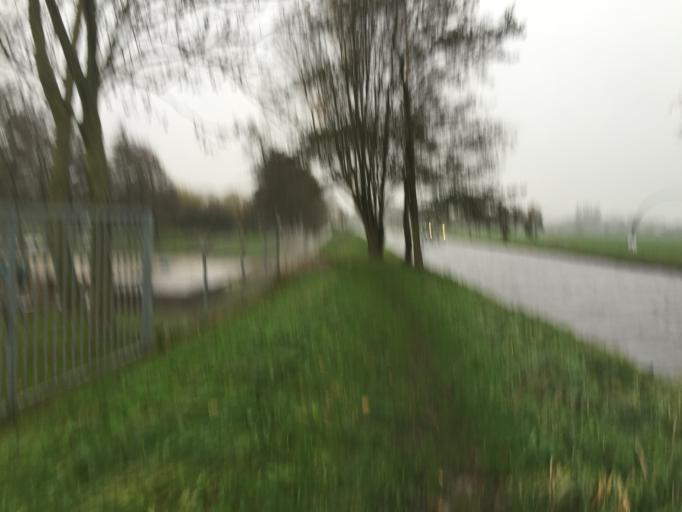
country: NL
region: Utrecht
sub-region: Gemeente Woerden
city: Woerden
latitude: 52.0944
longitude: 4.8620
